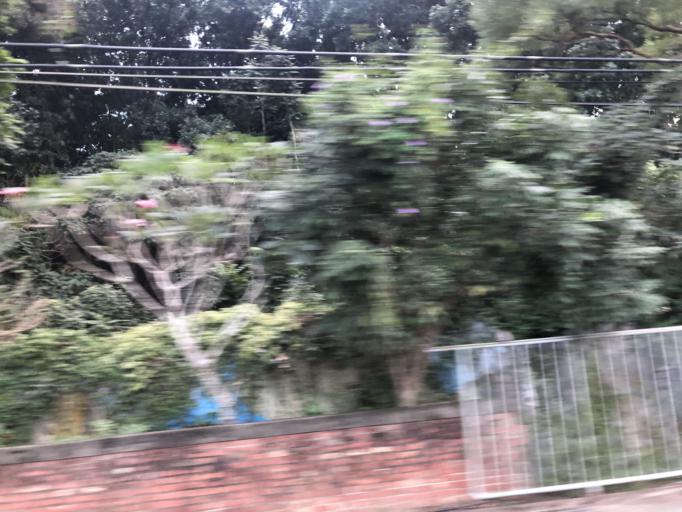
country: TW
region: Taiwan
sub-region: Tainan
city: Tainan
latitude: 23.0245
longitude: 120.3500
